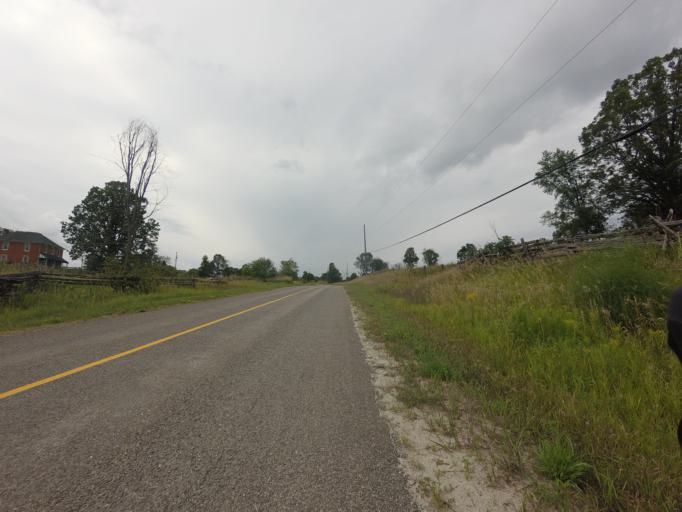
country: CA
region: Ontario
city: Perth
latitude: 44.8383
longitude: -76.5758
